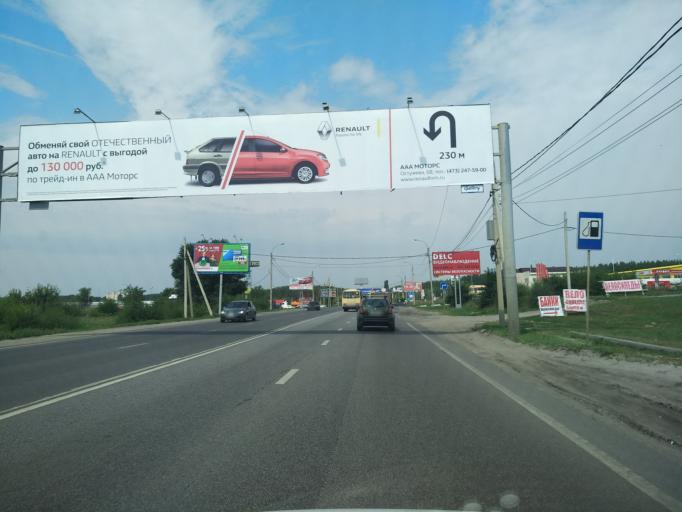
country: RU
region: Voronezj
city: Somovo
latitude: 51.6798
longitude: 39.2878
